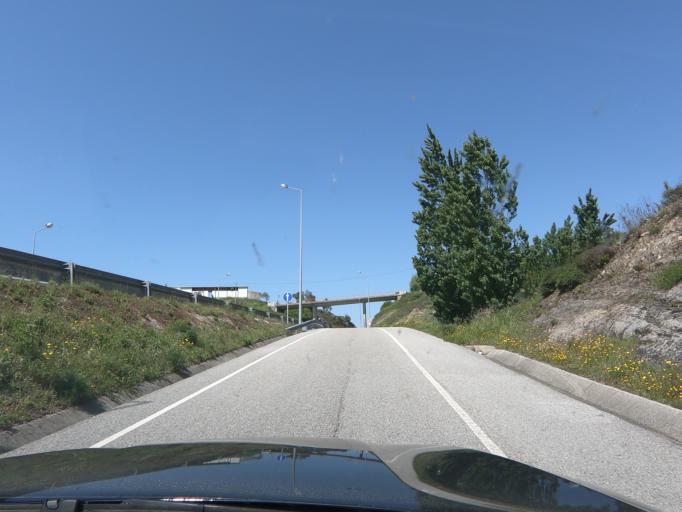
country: PT
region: Coimbra
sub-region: Vila Nova de Poiares
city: Poiares
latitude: 40.1763
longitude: -8.2677
